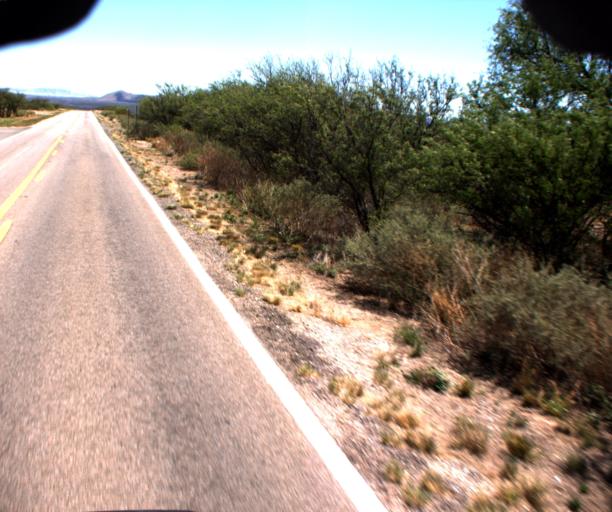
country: US
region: Arizona
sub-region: Cochise County
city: Huachuca City
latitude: 31.7205
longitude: -110.2250
